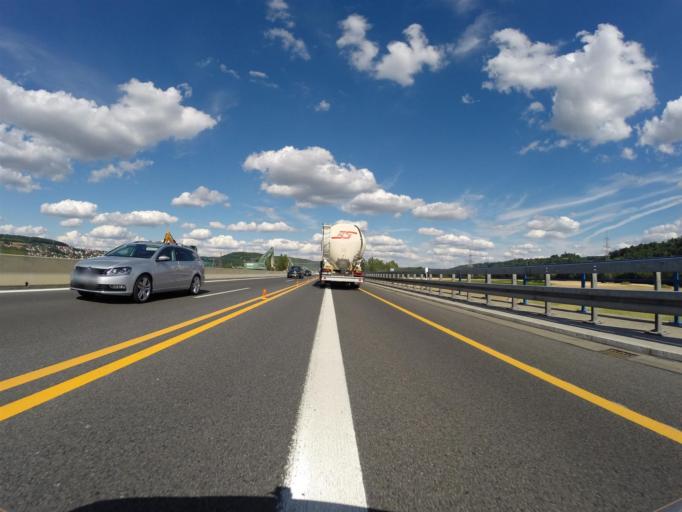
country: DE
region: Bavaria
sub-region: Regierungsbezirk Unterfranken
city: Eltmann
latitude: 49.9775
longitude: 10.6532
